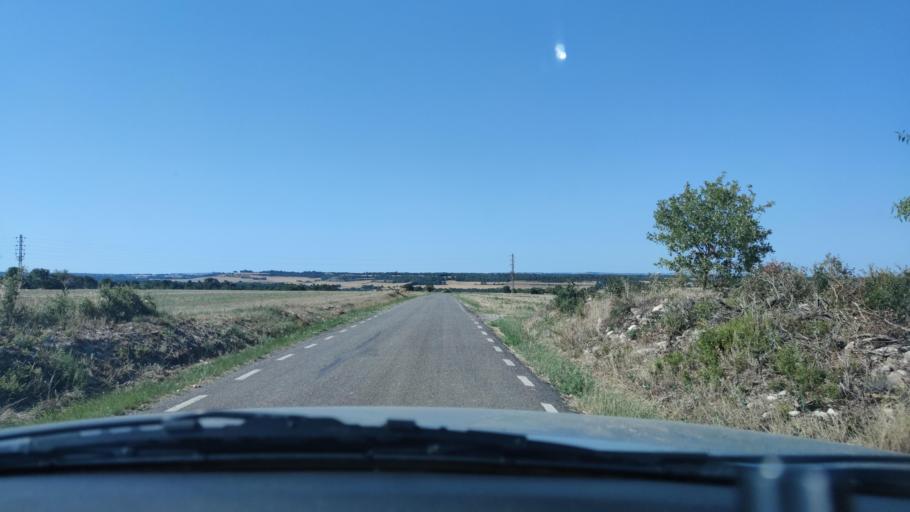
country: ES
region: Catalonia
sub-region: Provincia de Barcelona
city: Pujalt
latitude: 41.7010
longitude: 1.3834
